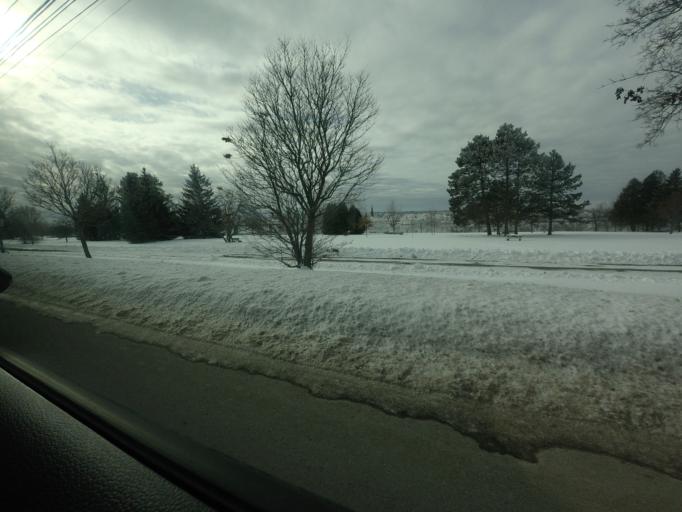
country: CA
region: New Brunswick
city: Fredericton
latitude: 45.9629
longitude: -66.6258
